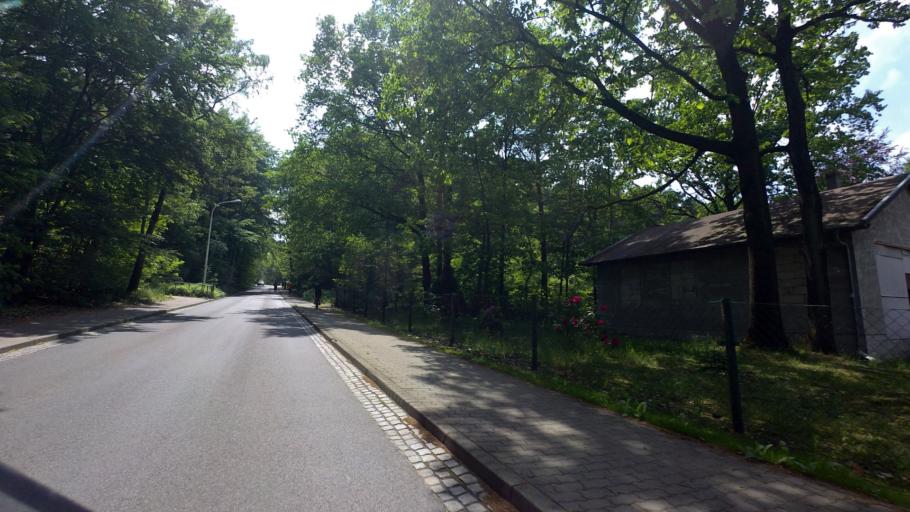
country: DE
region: Saxony
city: Weisswasser
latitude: 51.5014
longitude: 14.6151
